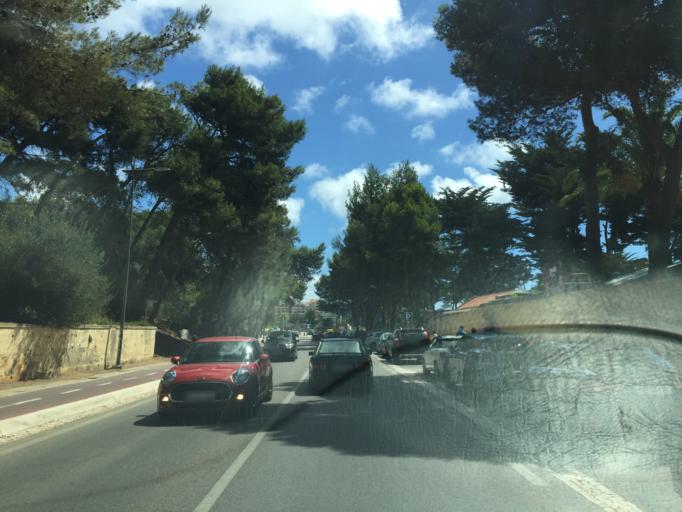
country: PT
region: Lisbon
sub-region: Cascais
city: Cascais
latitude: 38.6958
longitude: -9.4433
